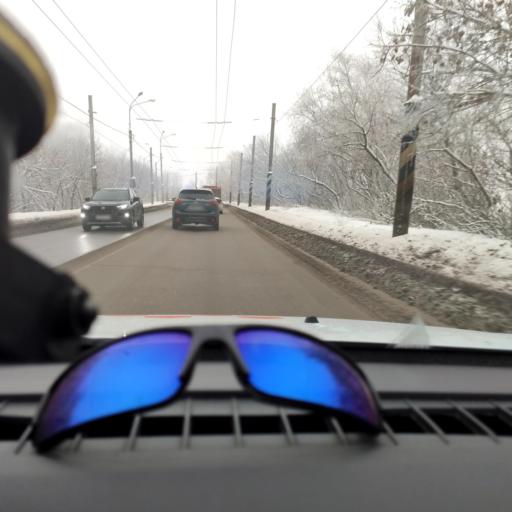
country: RU
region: Samara
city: Samara
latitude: 53.1495
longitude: 50.0942
